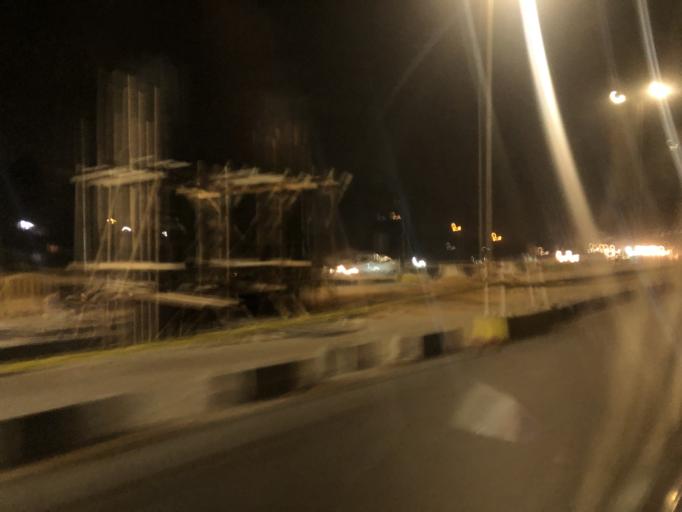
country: EG
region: Al Jizah
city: Al Jizah
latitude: 29.9814
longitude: 31.1199
